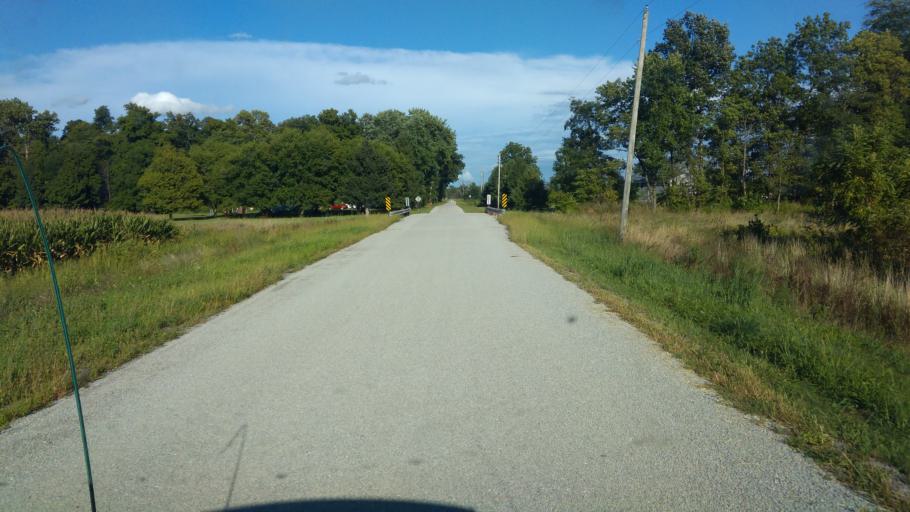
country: US
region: Ohio
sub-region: Hardin County
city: Forest
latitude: 40.7529
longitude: -83.5881
